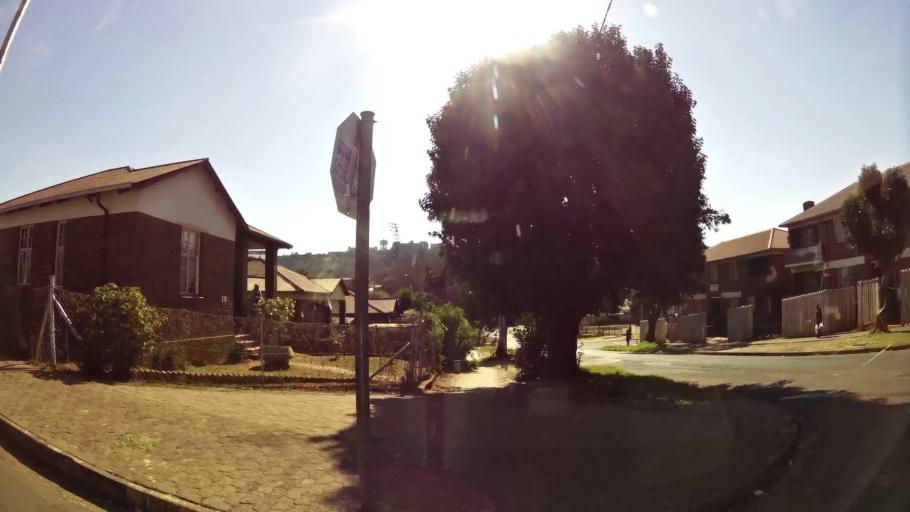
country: ZA
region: Gauteng
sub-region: City of Johannesburg Metropolitan Municipality
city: Johannesburg
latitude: -26.1952
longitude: 28.0680
